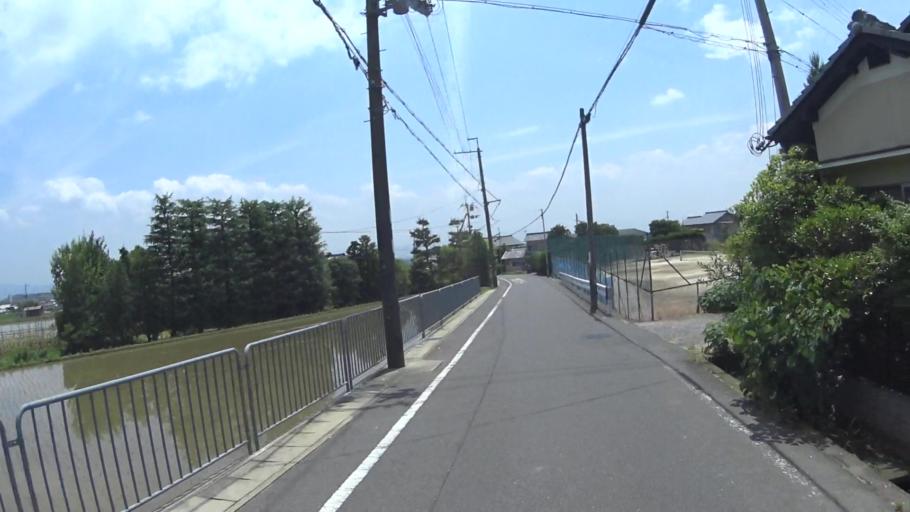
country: JP
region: Kyoto
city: Muko
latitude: 34.9621
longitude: 135.6599
